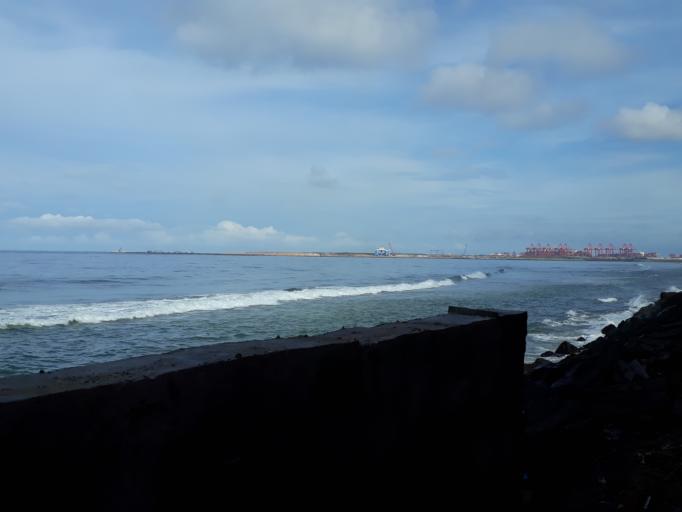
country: LK
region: Western
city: Colombo
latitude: 6.9119
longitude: 79.8479
